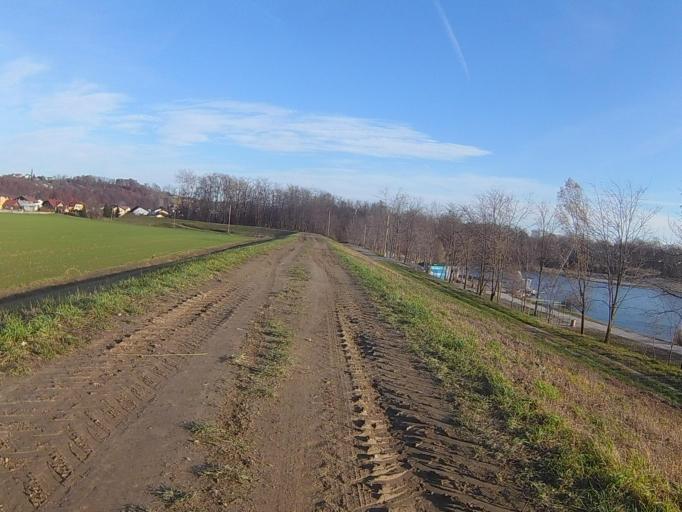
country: SI
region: Duplek
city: Spodnji Duplek
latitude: 46.5054
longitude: 15.7347
